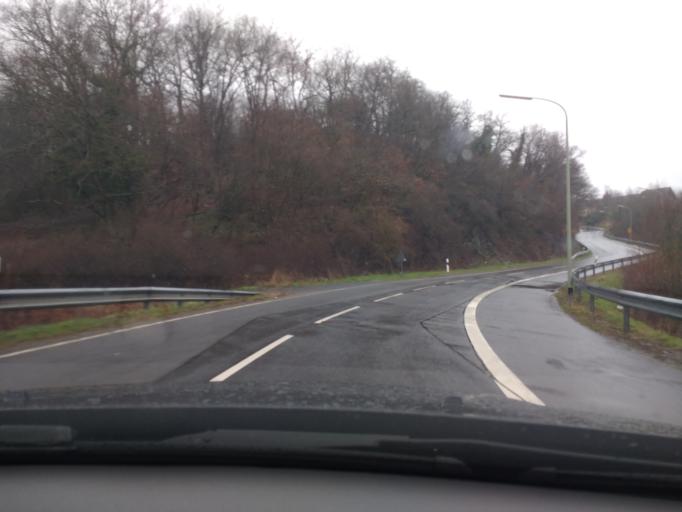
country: DE
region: Rheinland-Pfalz
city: Gusterath
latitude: 49.6960
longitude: 6.7145
